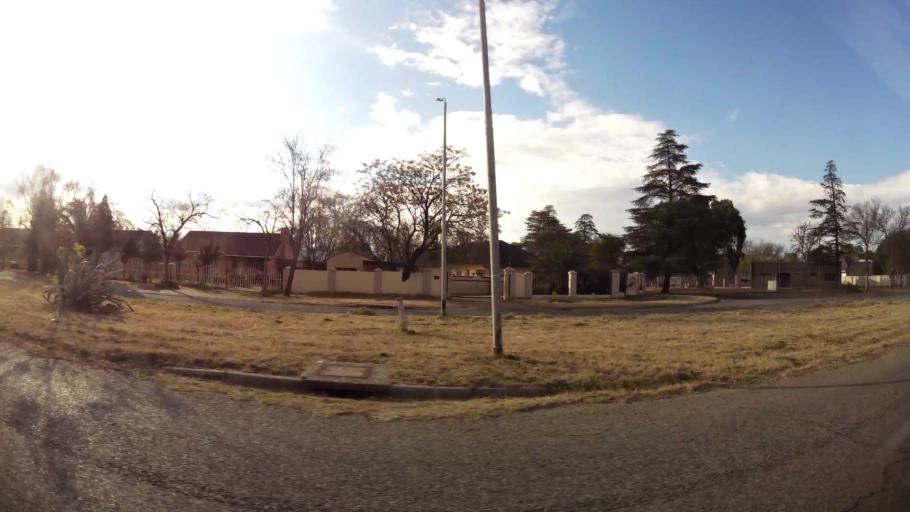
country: ZA
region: Orange Free State
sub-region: Lejweleputswa District Municipality
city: Welkom
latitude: -27.9868
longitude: 26.7199
